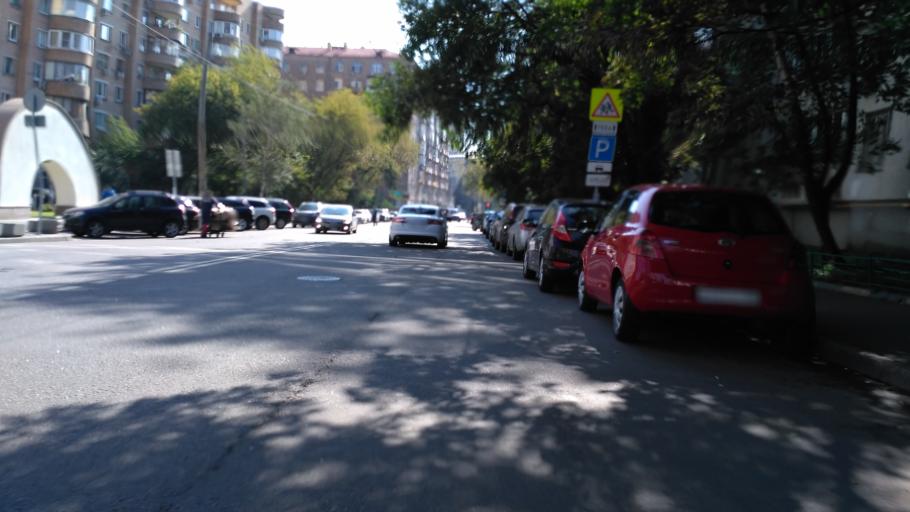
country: RU
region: Moscow
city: Lefortovo
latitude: 55.7741
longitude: 37.6735
